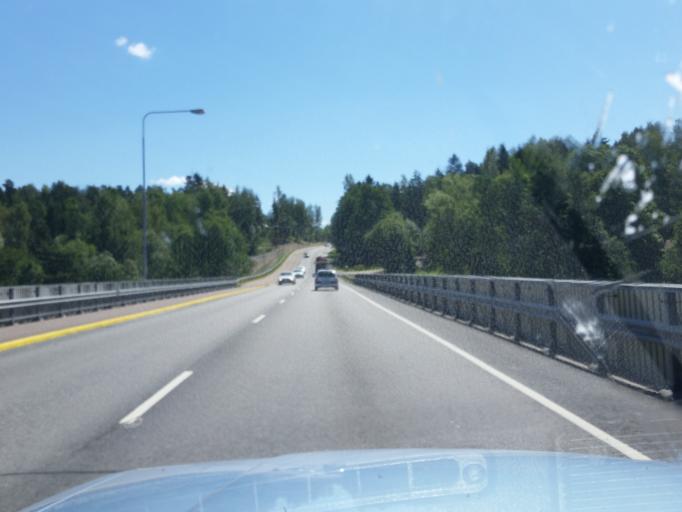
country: FI
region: Varsinais-Suomi
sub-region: Turku
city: Kaarina
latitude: 60.3964
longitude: 22.3905
